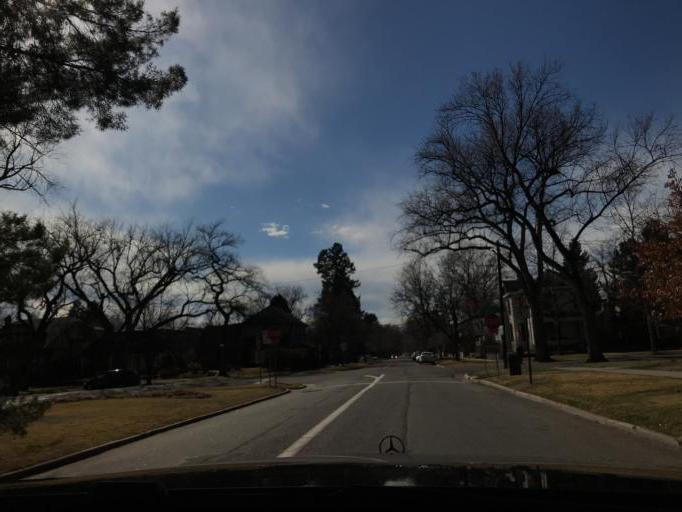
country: US
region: Colorado
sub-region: Denver County
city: Denver
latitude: 39.7273
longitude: -104.9653
